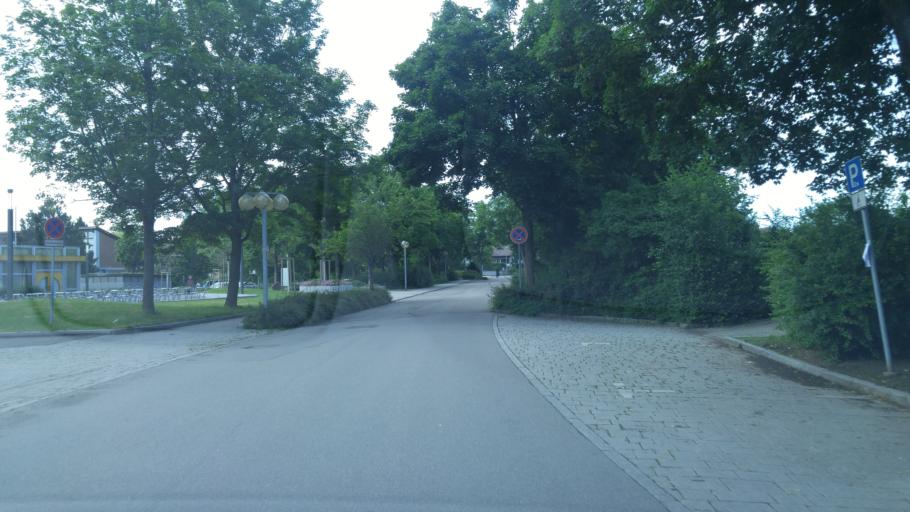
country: DE
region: Baden-Wuerttemberg
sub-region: Regierungsbezirk Stuttgart
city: Renningen
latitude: 48.7685
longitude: 8.9304
